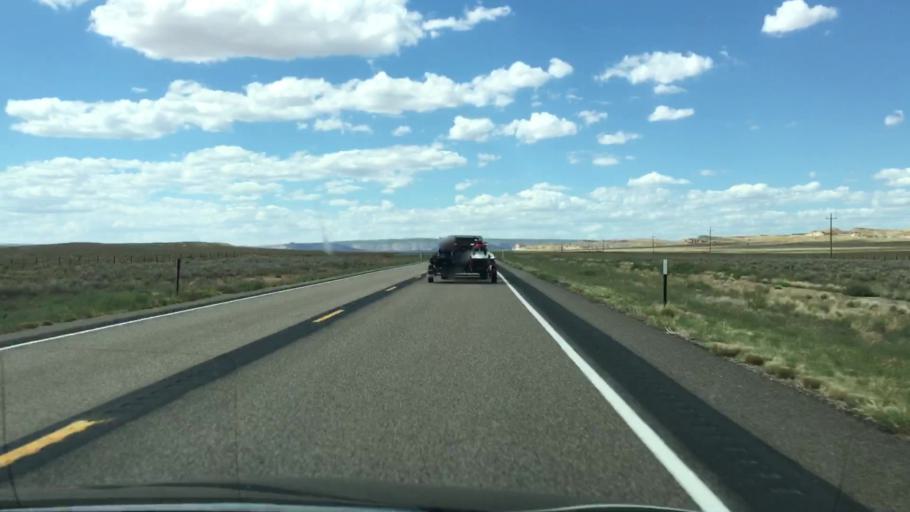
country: US
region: Arizona
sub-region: Coconino County
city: Page
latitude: 37.1034
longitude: -111.8228
